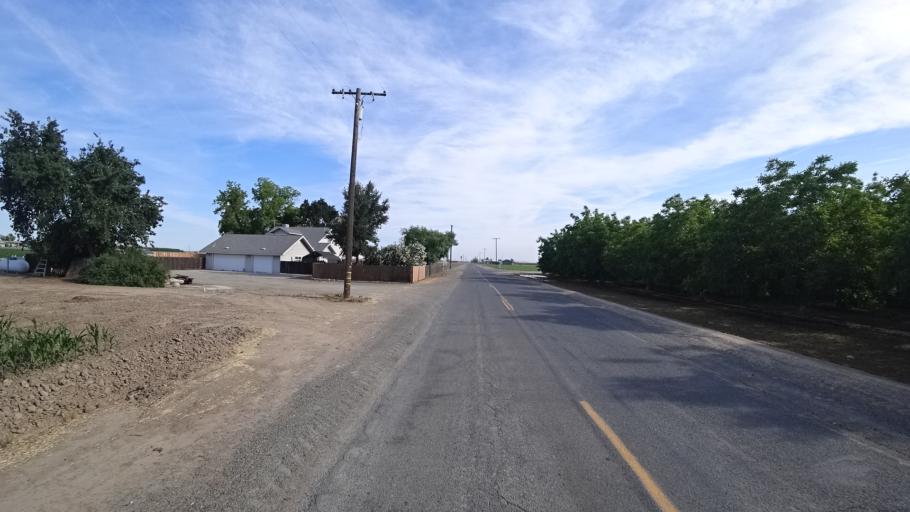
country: US
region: California
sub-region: Kings County
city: Hanford
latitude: 36.3712
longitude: -119.5470
